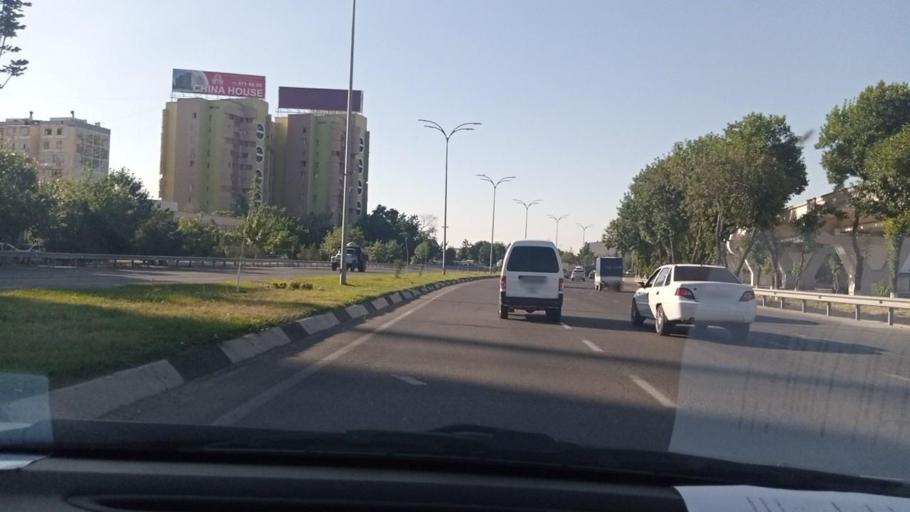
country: UZ
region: Toshkent Shahri
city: Bektemir
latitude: 41.2901
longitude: 69.3585
